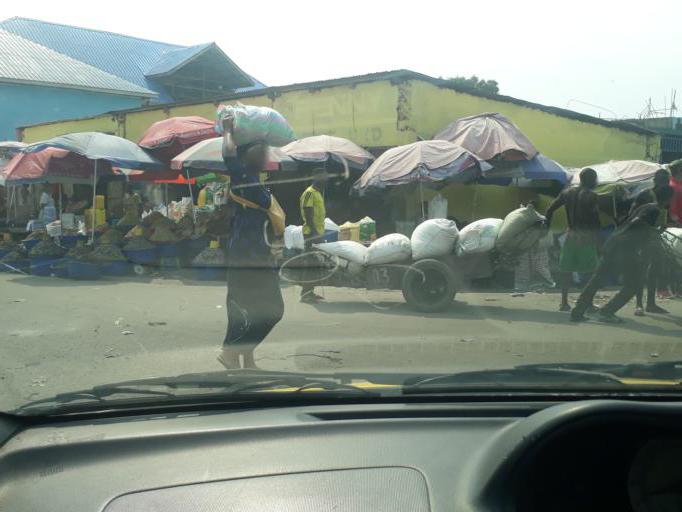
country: CD
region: Kinshasa
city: Kinshasa
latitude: -4.3276
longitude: 15.3194
